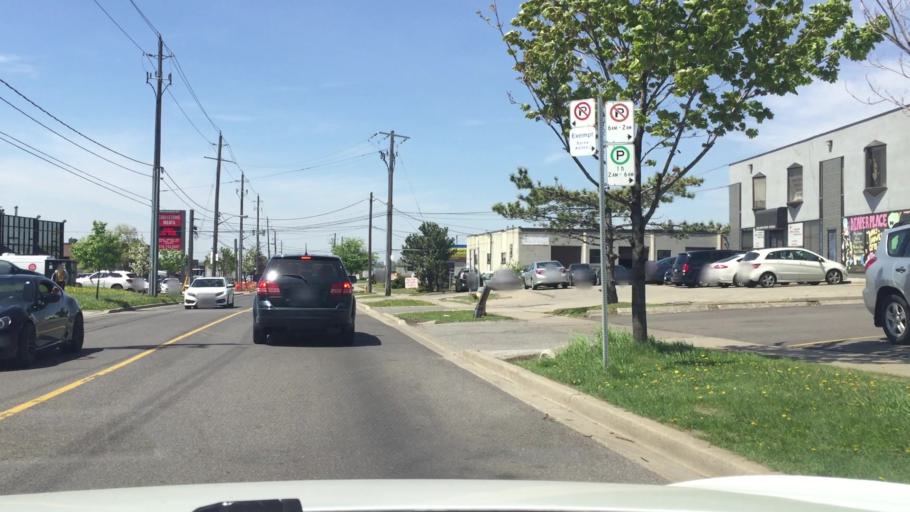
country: CA
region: Ontario
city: Concord
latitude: 43.7481
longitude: -79.5206
